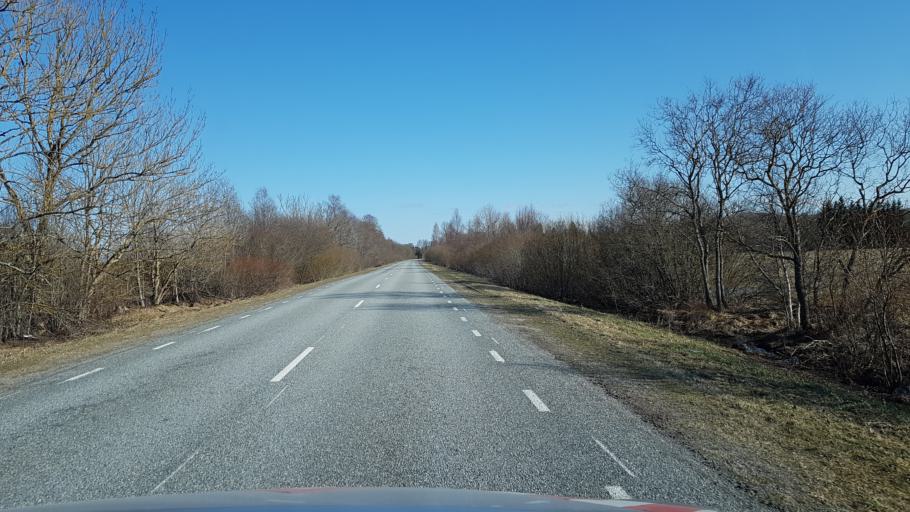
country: EE
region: Laeaene-Virumaa
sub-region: Haljala vald
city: Haljala
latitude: 59.4987
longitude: 26.1349
